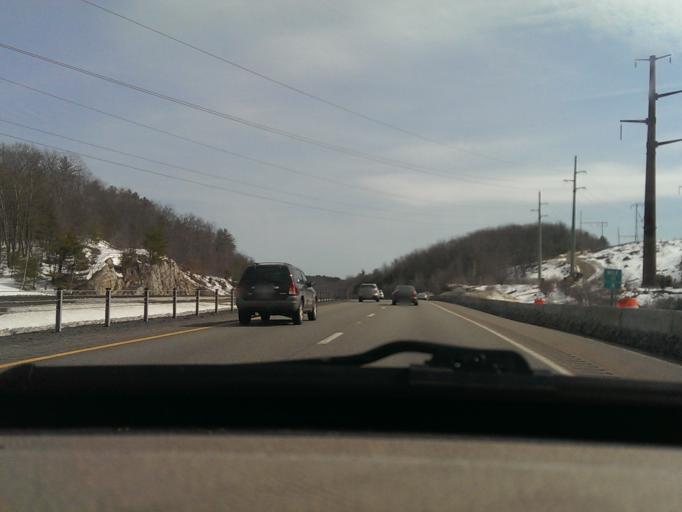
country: US
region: Massachusetts
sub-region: Worcester County
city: Sutton
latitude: 42.1401
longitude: -71.7125
